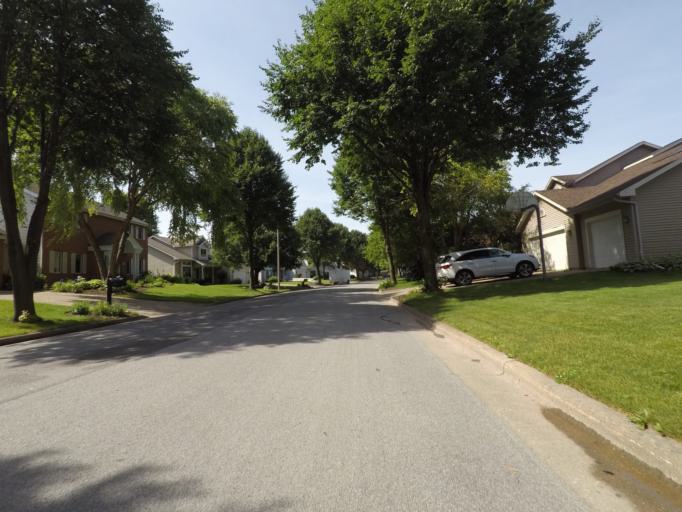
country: US
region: Wisconsin
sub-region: Dane County
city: Middleton
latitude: 43.0792
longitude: -89.5143
